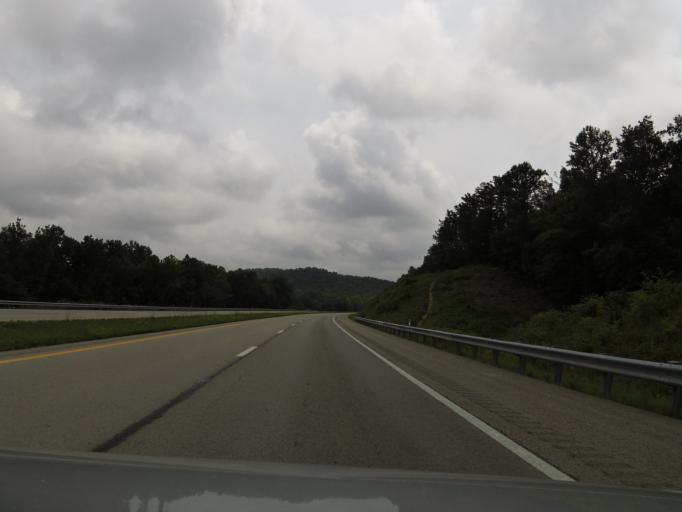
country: US
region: Kentucky
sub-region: Ohio County
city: Oak Grove
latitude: 37.3883
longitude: -86.6791
